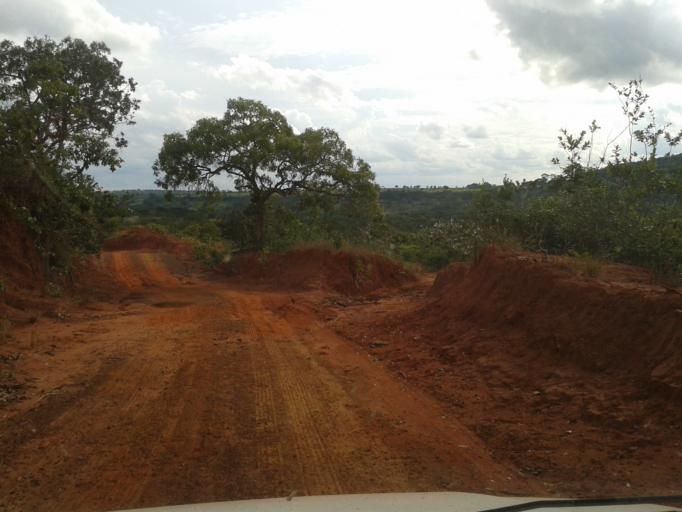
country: BR
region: Minas Gerais
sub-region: Campina Verde
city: Campina Verde
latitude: -19.4379
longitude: -49.5826
